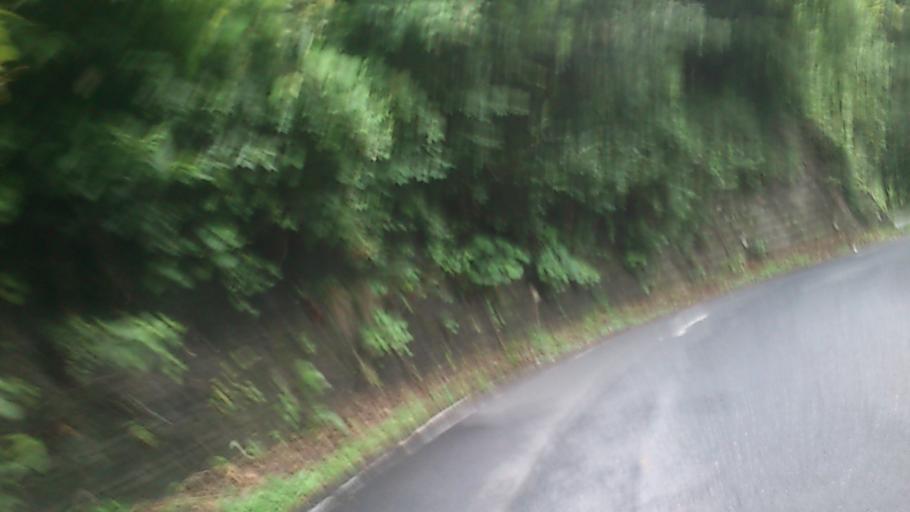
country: JP
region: Ibaraki
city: Omiya
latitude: 36.6223
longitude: 140.3614
